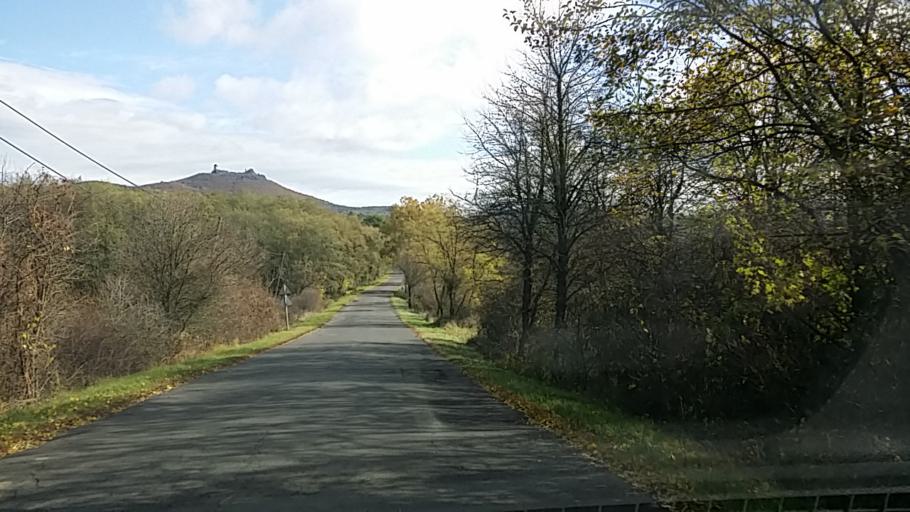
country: HU
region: Borsod-Abauj-Zemplen
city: Gonc
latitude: 48.3847
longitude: 21.3071
